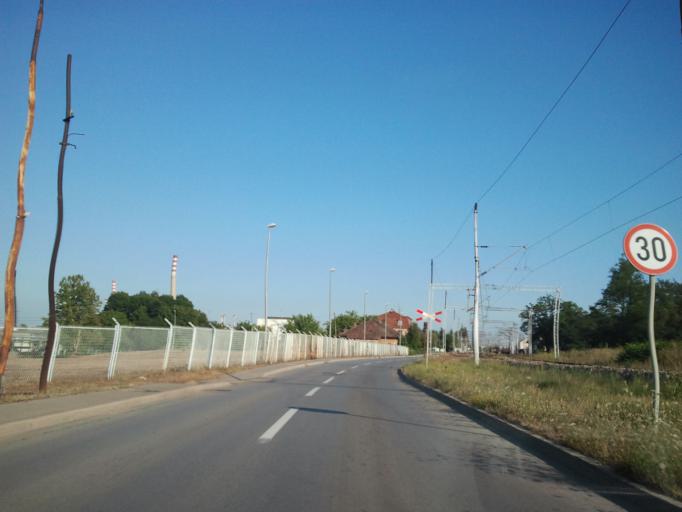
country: HR
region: Sisacko-Moslavacka
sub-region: Grad Sisak
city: Sisak
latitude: 45.4628
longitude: 16.3852
